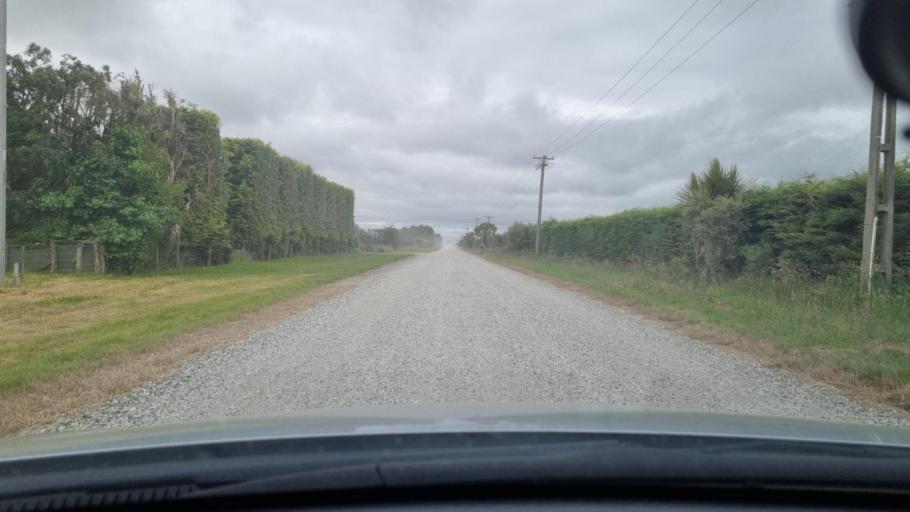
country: NZ
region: Southland
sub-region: Invercargill City
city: Invercargill
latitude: -46.3760
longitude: 168.2985
